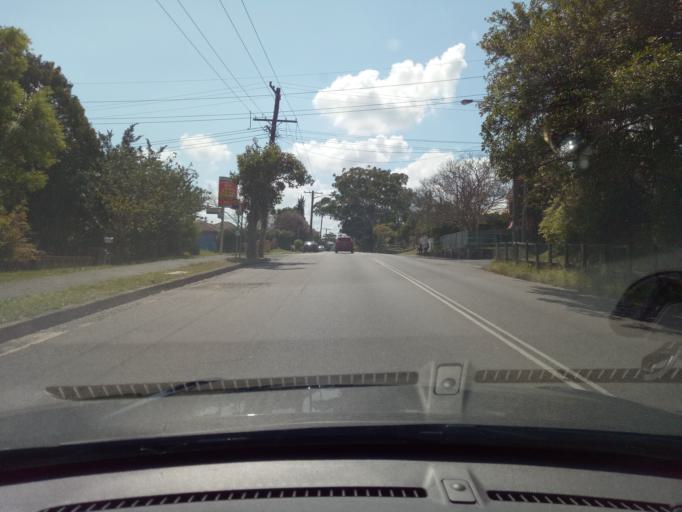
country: AU
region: New South Wales
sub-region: Gosford Shire
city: Gosford
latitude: -33.4154
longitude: 151.3442
